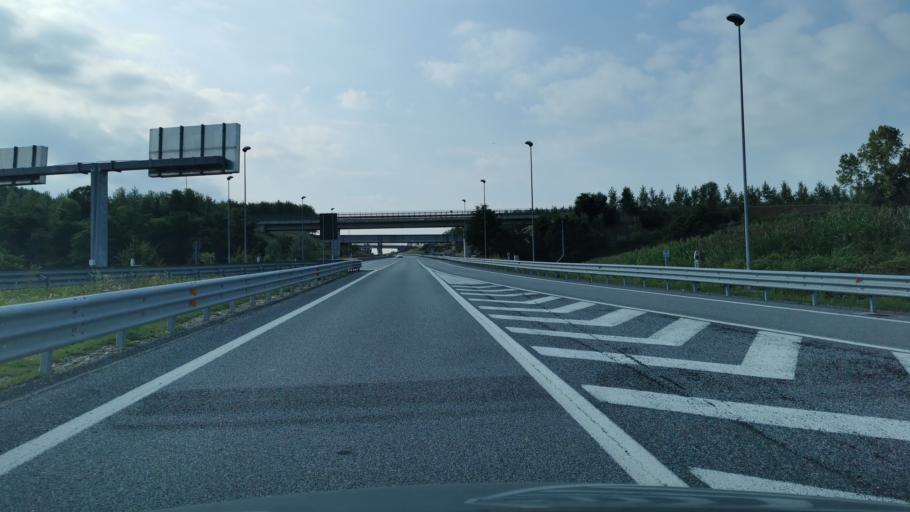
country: IT
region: Piedmont
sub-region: Provincia di Cuneo
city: Cuneo
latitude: 44.4227
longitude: 7.5901
